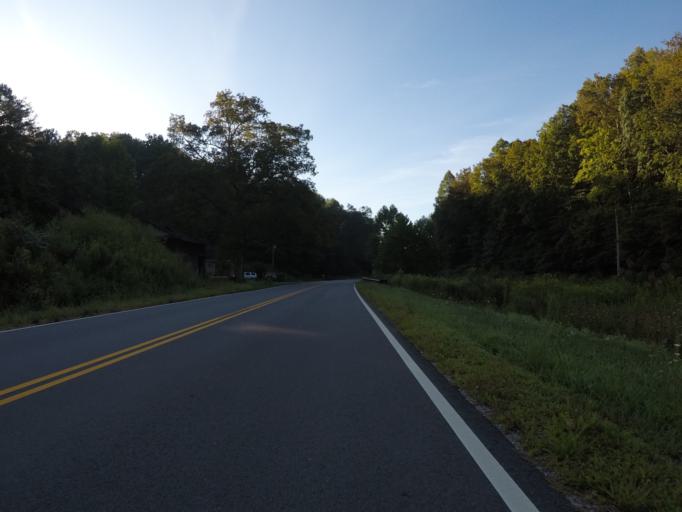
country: US
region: Ohio
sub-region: Lawrence County
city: Coal Grove
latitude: 38.6043
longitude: -82.5701
